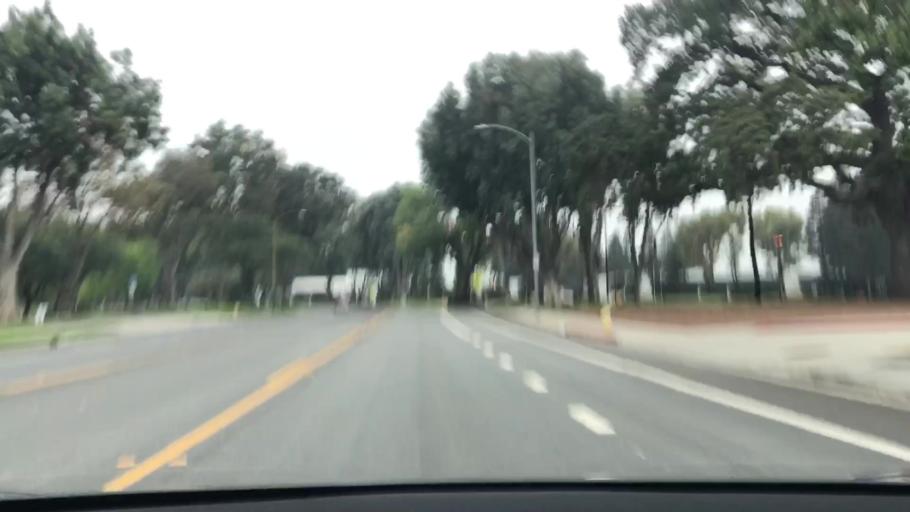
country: US
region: California
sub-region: Santa Clara County
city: Seven Trees
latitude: 37.2366
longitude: -121.7794
